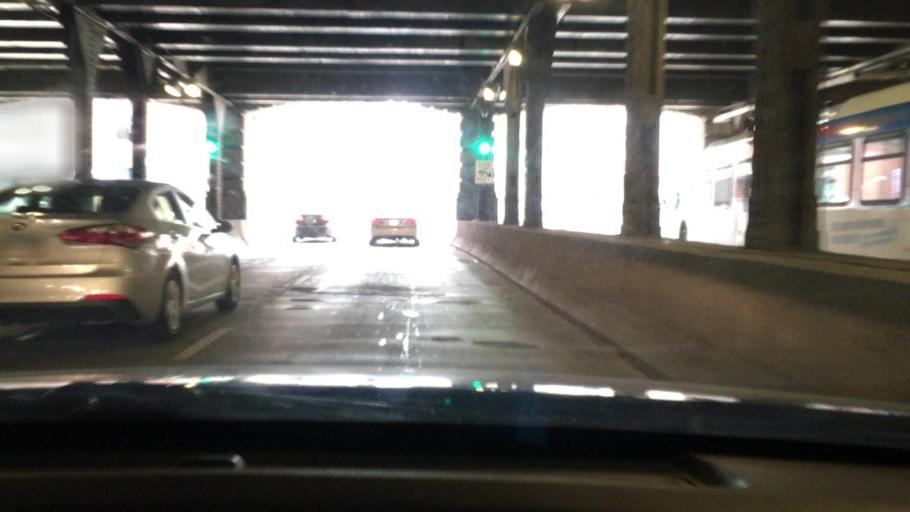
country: US
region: Illinois
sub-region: Cook County
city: Chicago
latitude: 41.8832
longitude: -87.6402
